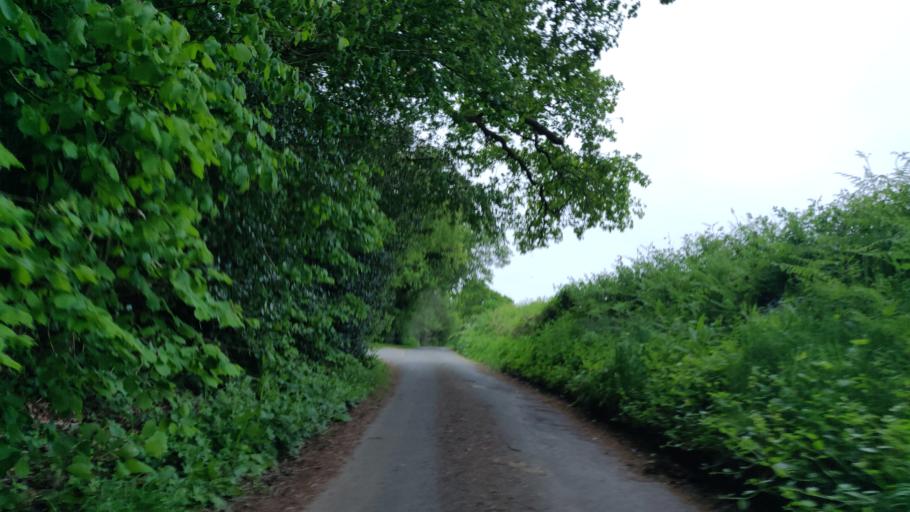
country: GB
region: England
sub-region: West Sussex
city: Southwater
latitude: 51.0270
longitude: -0.3312
